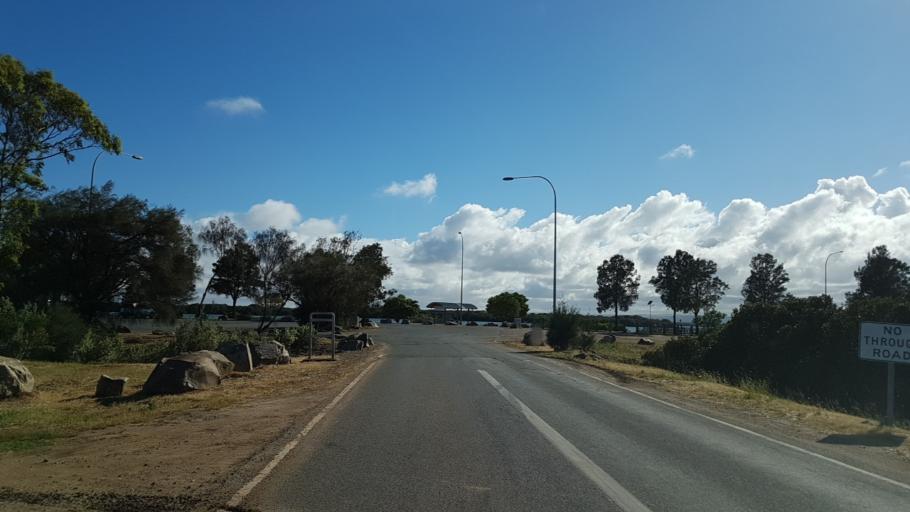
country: AU
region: South Australia
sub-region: Port Adelaide Enfield
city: Birkenhead
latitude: -34.8062
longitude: 138.5395
